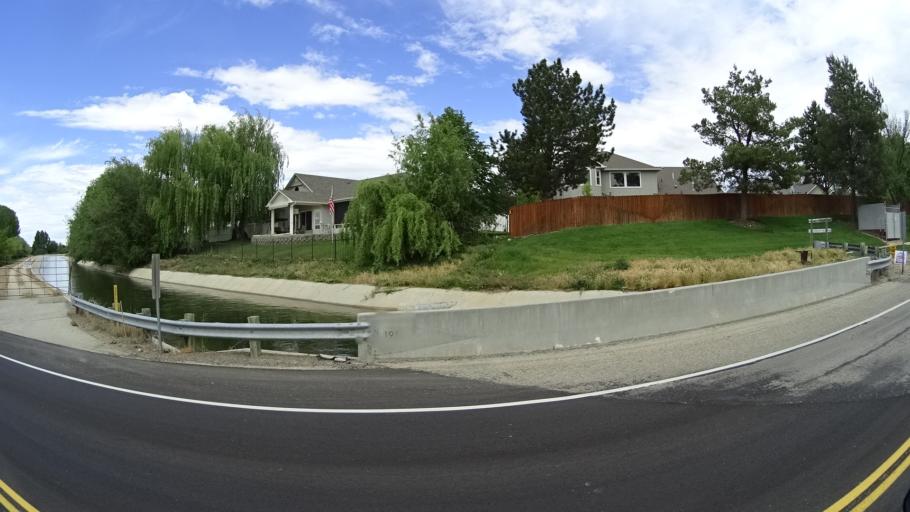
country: US
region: Idaho
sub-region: Ada County
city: Meridian
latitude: 43.5757
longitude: -116.3614
